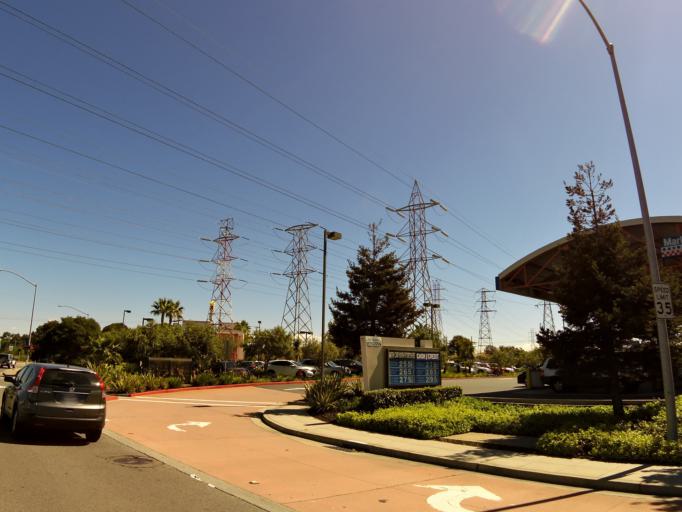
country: US
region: California
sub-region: San Mateo County
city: Millbrae
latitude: 37.6007
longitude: -122.3835
